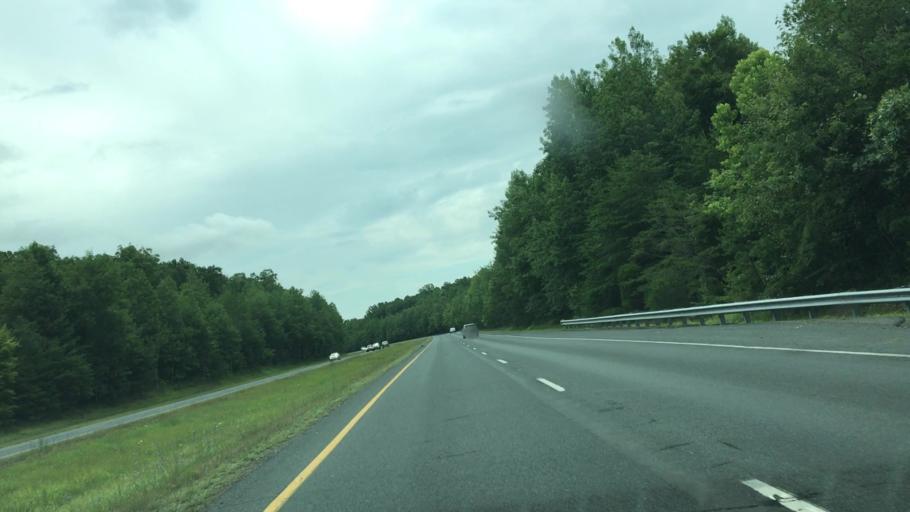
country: US
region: Virginia
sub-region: Prince William County
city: Buckhall
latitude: 38.6855
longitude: -77.3749
